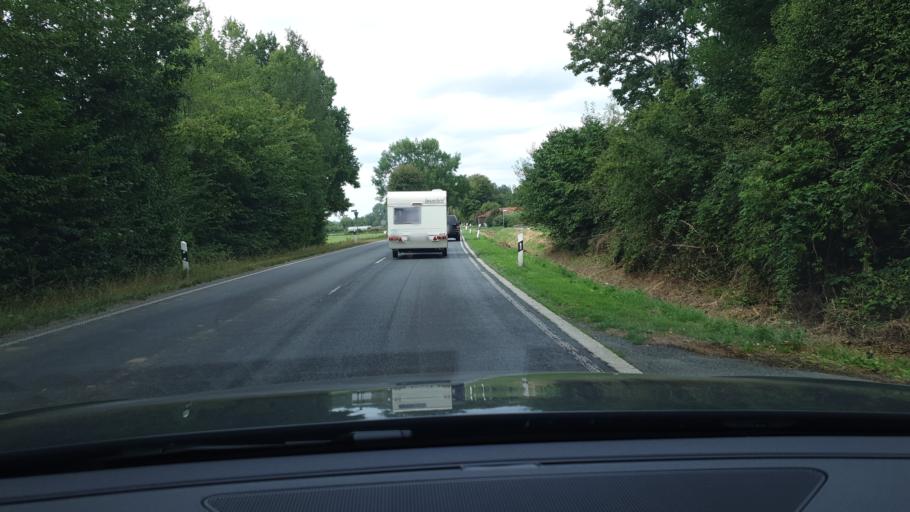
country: DE
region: North Rhine-Westphalia
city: Straelen
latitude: 51.4353
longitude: 6.2417
